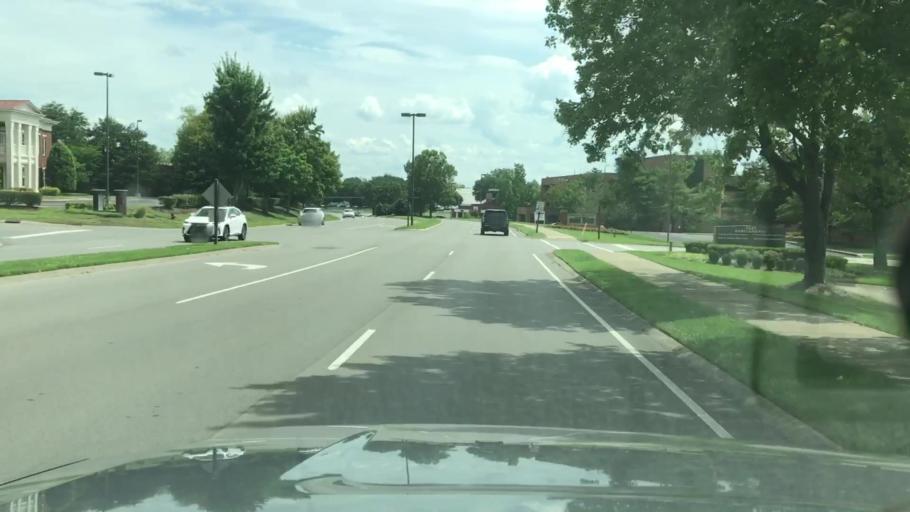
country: US
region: Tennessee
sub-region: Williamson County
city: Brentwood
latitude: 36.0342
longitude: -86.8021
